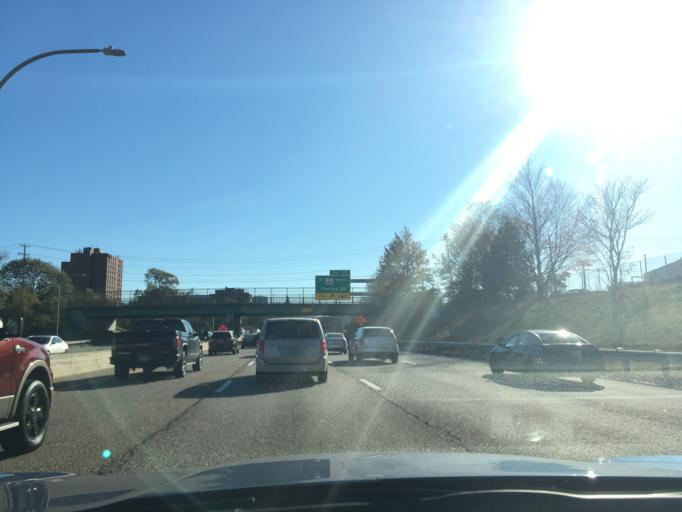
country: US
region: Rhode Island
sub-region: Providence County
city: Providence
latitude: 41.8420
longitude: -71.4111
